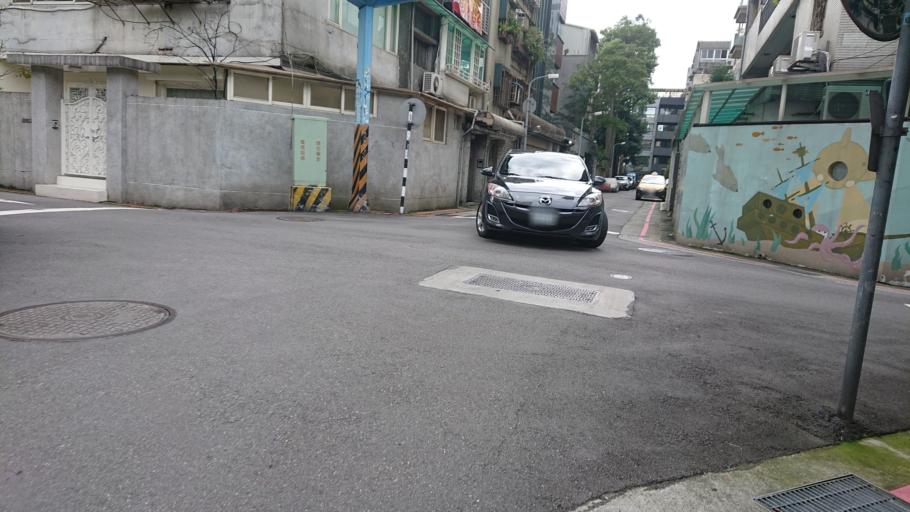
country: TW
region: Taipei
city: Taipei
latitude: 25.0397
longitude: 121.5361
